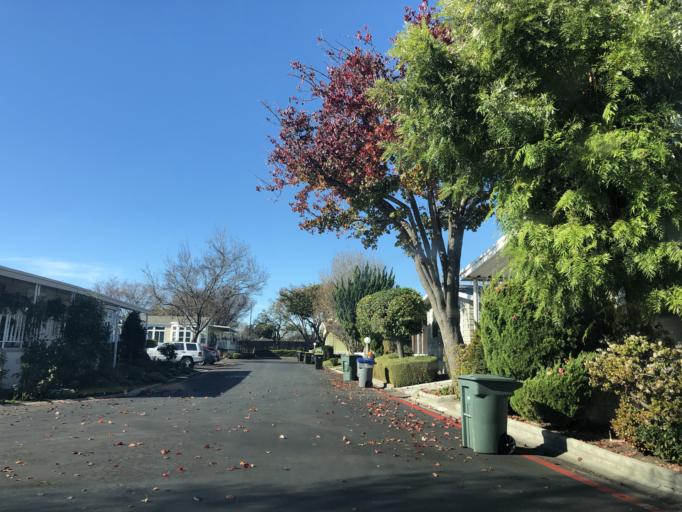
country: US
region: California
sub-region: Santa Clara County
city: Sunnyvale
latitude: 37.4024
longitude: -122.0199
